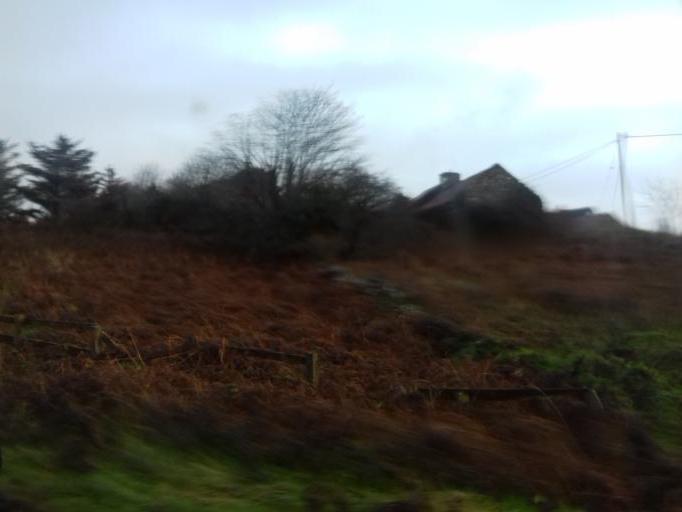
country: IE
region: Ulster
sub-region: County Donegal
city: Buncrana
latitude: 55.1726
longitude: -7.5821
